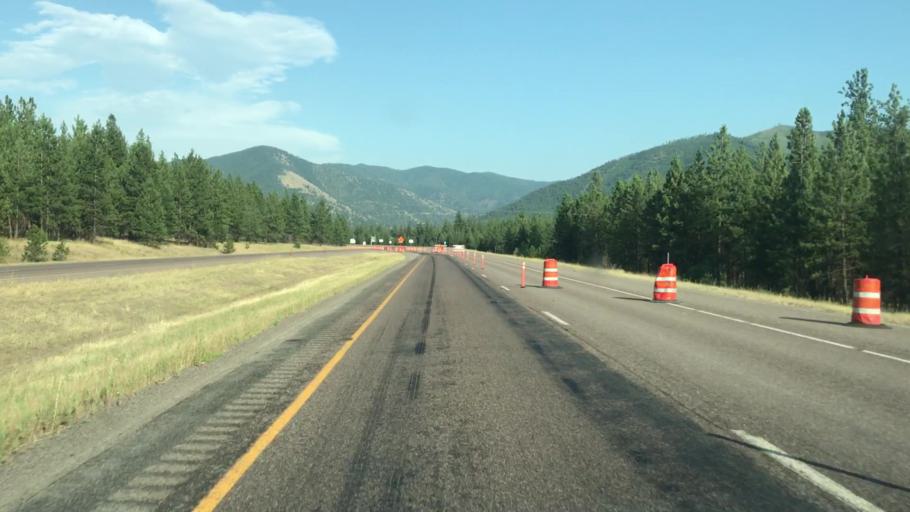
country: US
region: Montana
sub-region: Mineral County
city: Superior
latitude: 47.0142
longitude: -114.7309
